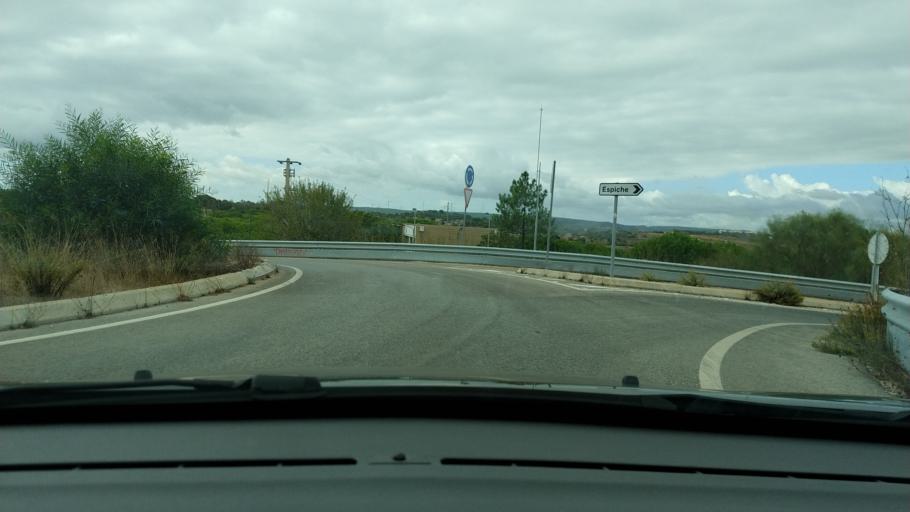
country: PT
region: Faro
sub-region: Lagos
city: Lagos
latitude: 37.0998
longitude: -8.7478
